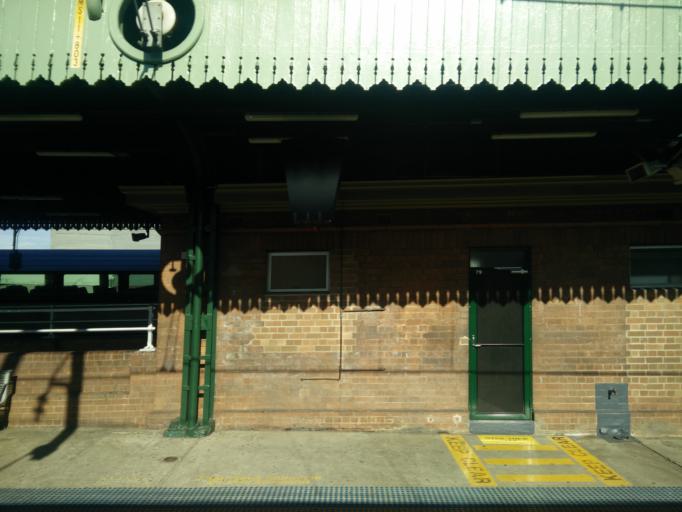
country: AU
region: New South Wales
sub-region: Strathfield
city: Homebush
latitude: -33.8720
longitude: 151.0943
